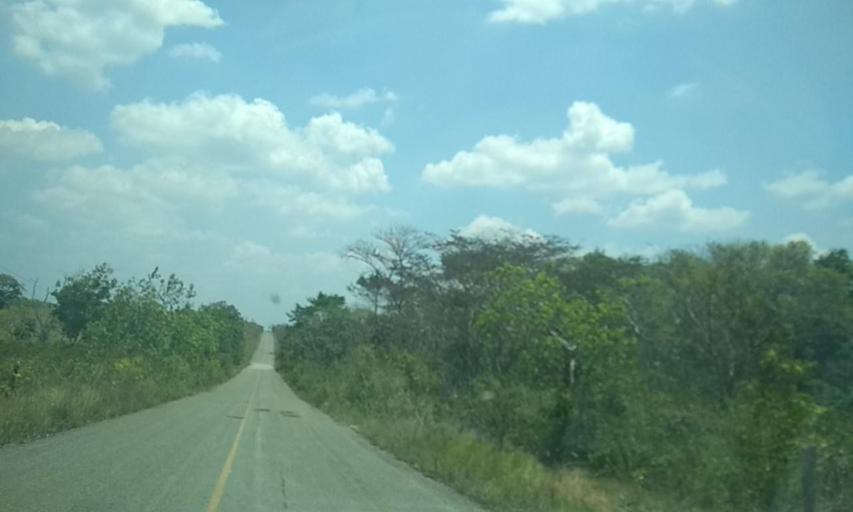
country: MX
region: Tabasco
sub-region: Huimanguillo
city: Francisco Rueda
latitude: 17.8209
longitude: -93.8713
